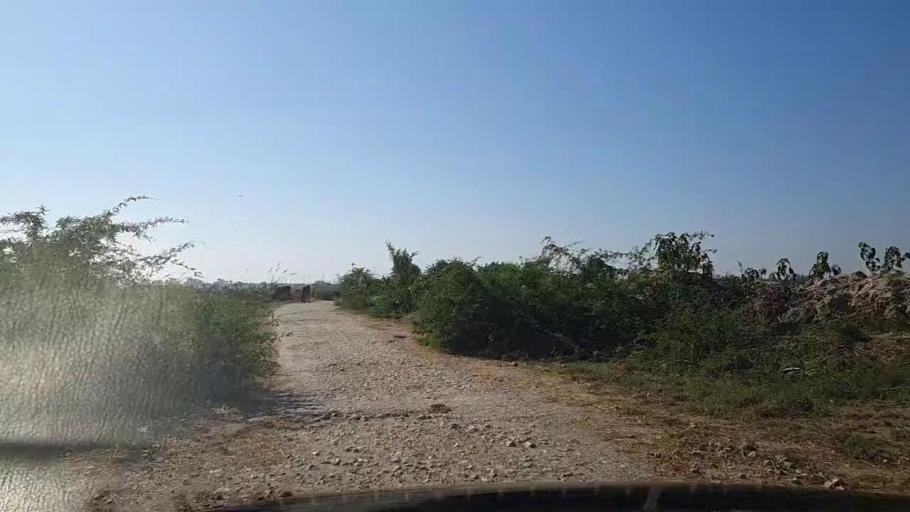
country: PK
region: Sindh
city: Thatta
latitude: 24.7143
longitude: 67.9194
